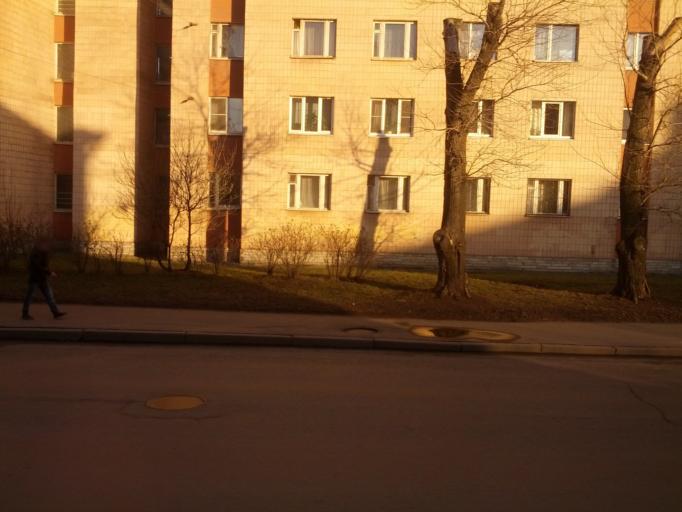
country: RU
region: St.-Petersburg
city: Centralniy
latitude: 59.9374
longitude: 30.4084
